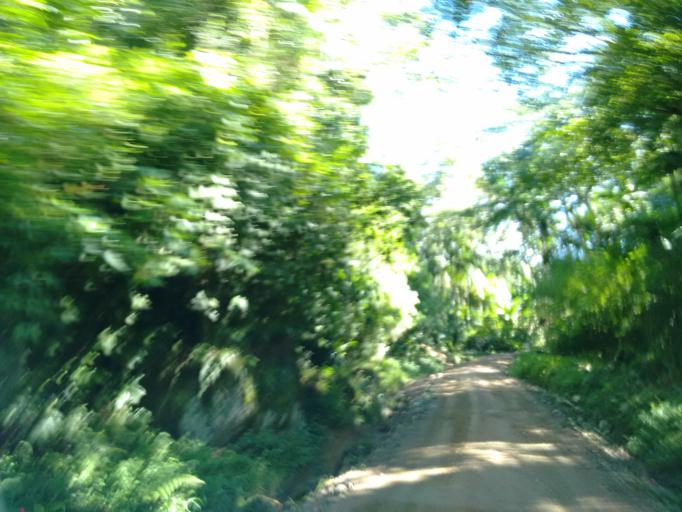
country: BR
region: Santa Catarina
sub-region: Pomerode
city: Pomerode
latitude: -26.7534
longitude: -49.1899
